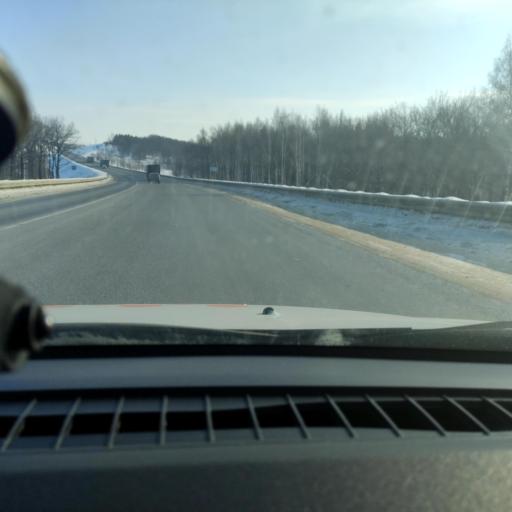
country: RU
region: Samara
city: Novosemeykino
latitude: 53.3597
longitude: 50.4398
